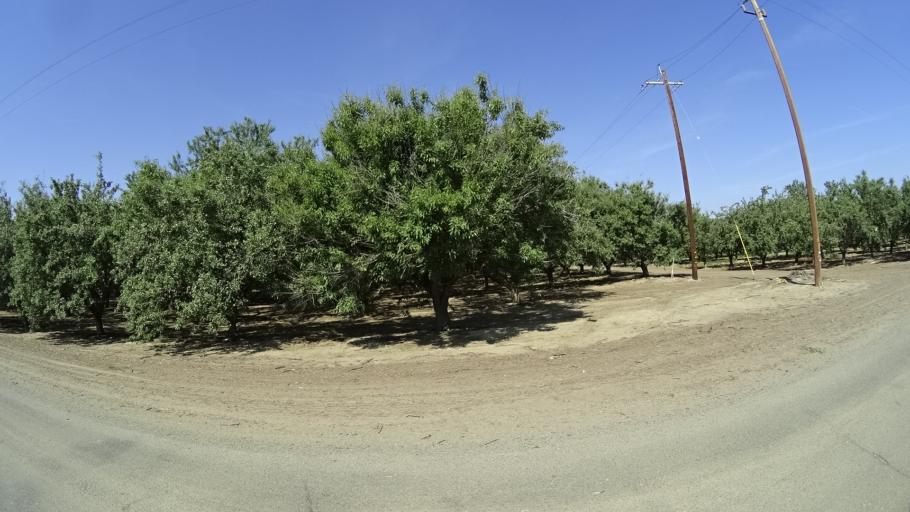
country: US
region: California
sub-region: Kings County
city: Kettleman City
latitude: 36.0650
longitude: -120.0036
